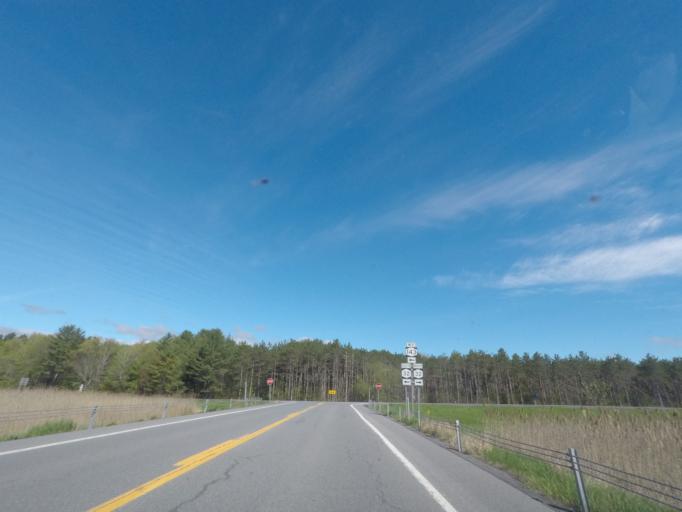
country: US
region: New York
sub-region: Albany County
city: Ravena
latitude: 42.5065
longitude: -73.9512
